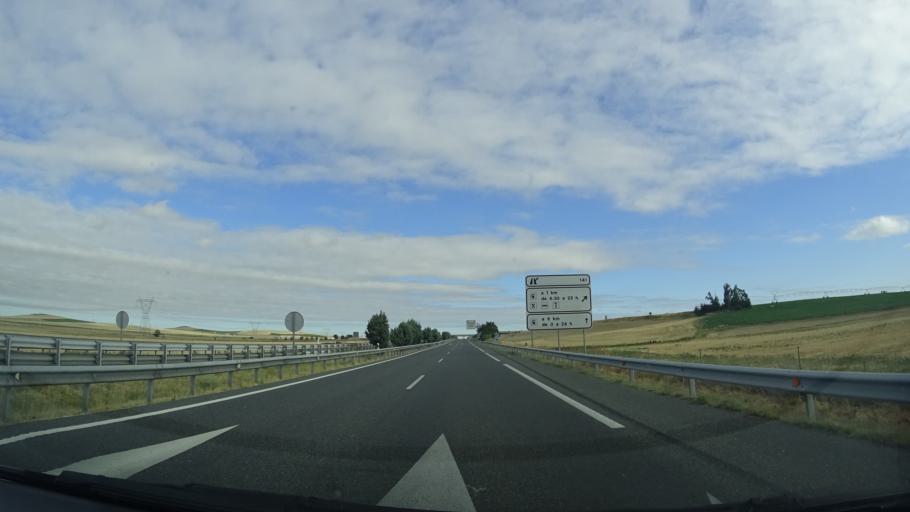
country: ES
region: Castille and Leon
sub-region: Provincia de Valladolid
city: Ataquines
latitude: 41.1711
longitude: -4.8023
